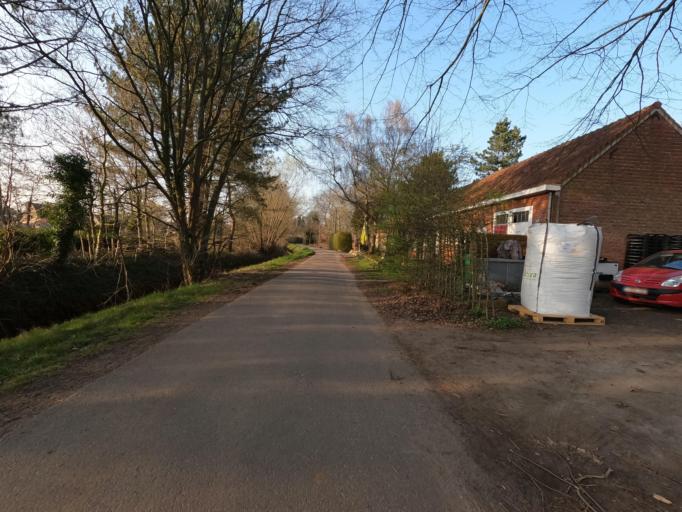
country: BE
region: Flanders
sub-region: Provincie Antwerpen
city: Hulshout
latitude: 51.0488
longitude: 4.7834
